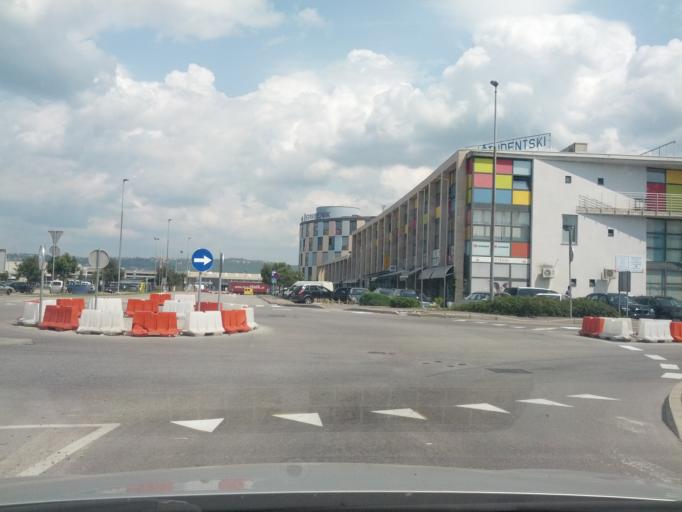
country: SI
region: Koper-Capodistria
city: Koper
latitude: 45.5453
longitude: 13.7396
